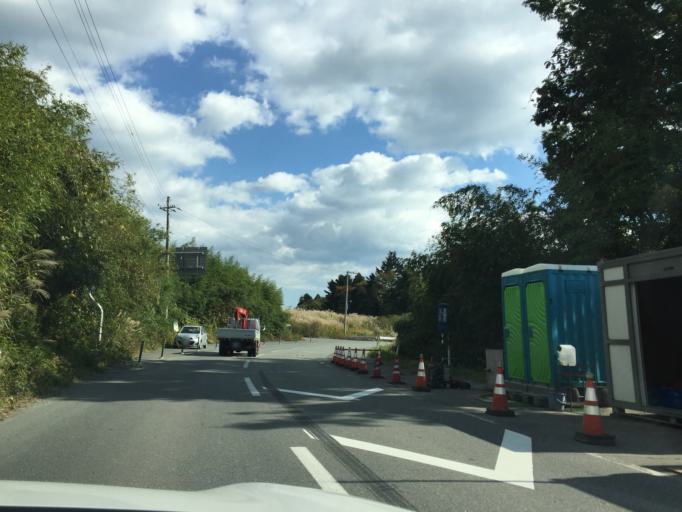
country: JP
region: Fukushima
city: Namie
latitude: 37.3731
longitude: 140.9915
